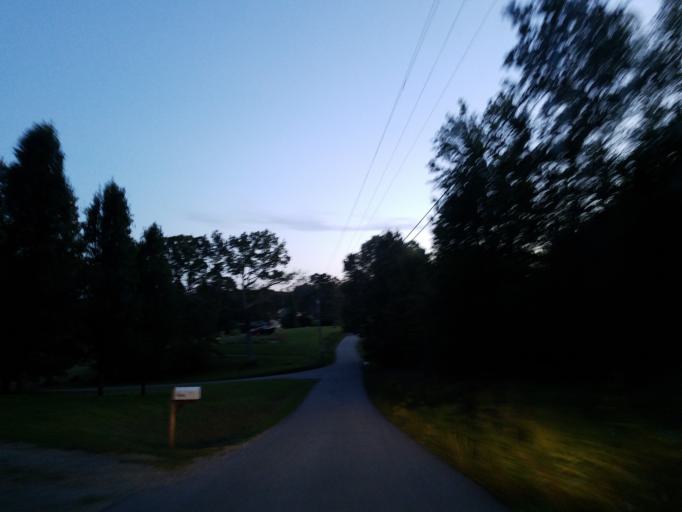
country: US
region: Georgia
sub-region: Dawson County
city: Dawsonville
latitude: 34.5298
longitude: -84.1755
